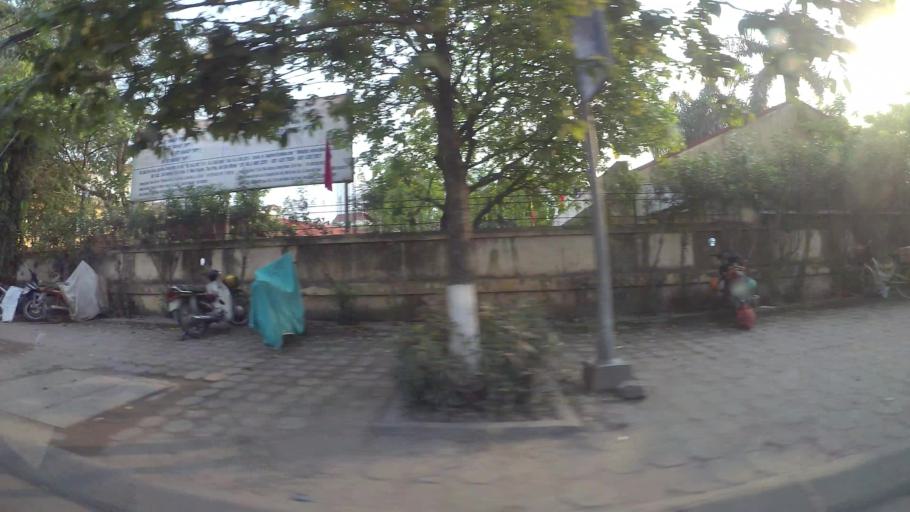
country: VN
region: Ha Noi
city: Thanh Xuan
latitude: 20.9781
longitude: 105.8231
